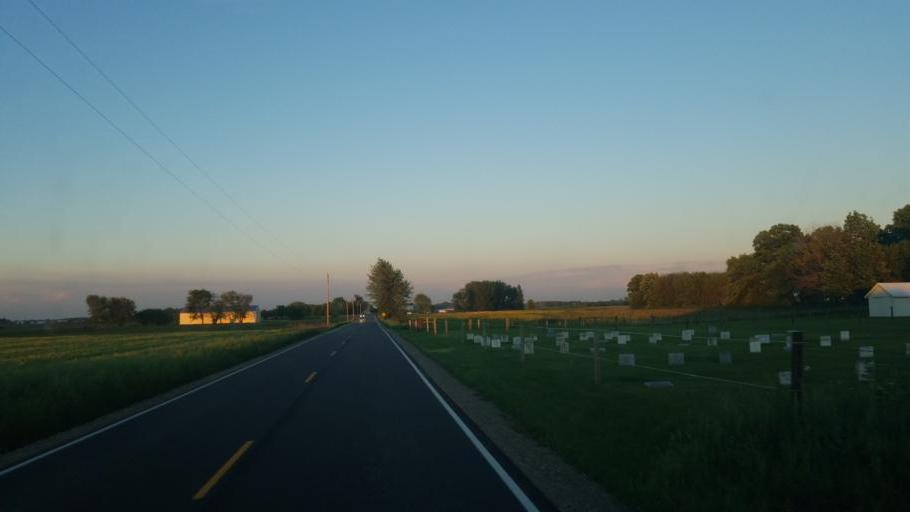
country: US
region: Indiana
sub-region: Elkhart County
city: Nappanee
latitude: 41.3614
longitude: -85.9896
